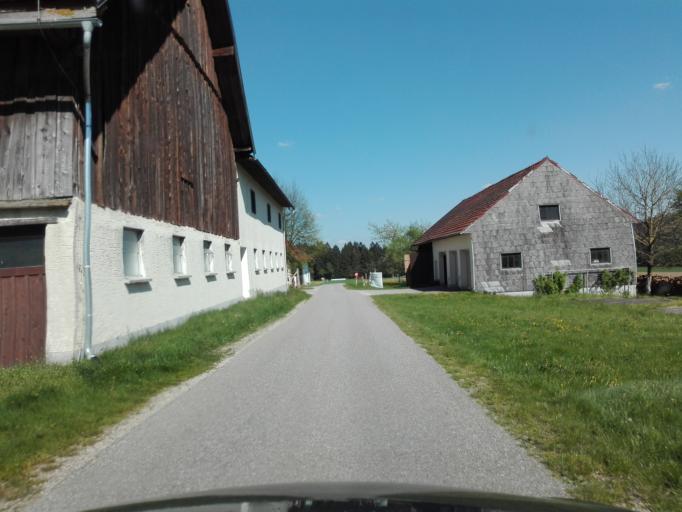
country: DE
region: Bavaria
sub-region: Lower Bavaria
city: Obernzell
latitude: 48.4399
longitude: 13.7030
